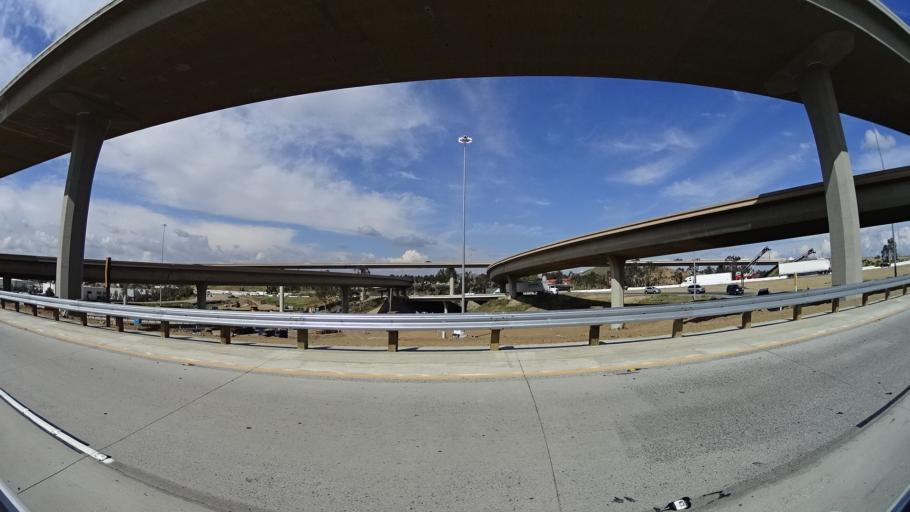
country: US
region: California
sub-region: Riverside County
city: Corona
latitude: 33.8804
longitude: -117.5483
